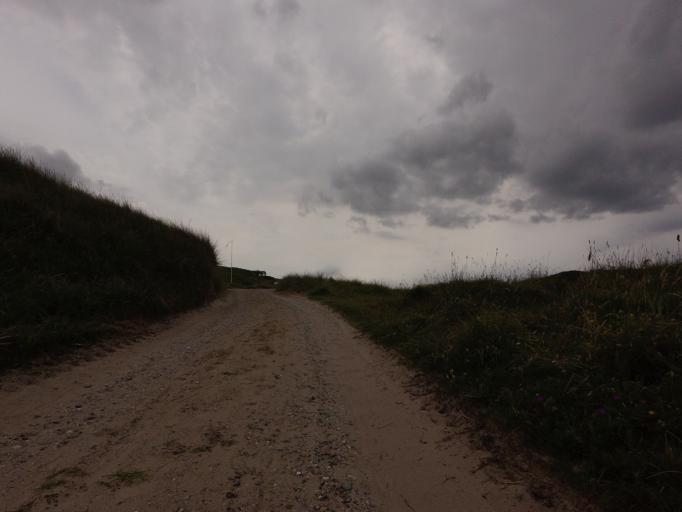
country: DK
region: North Denmark
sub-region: Jammerbugt Kommune
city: Pandrup
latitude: 57.3089
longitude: 9.6472
